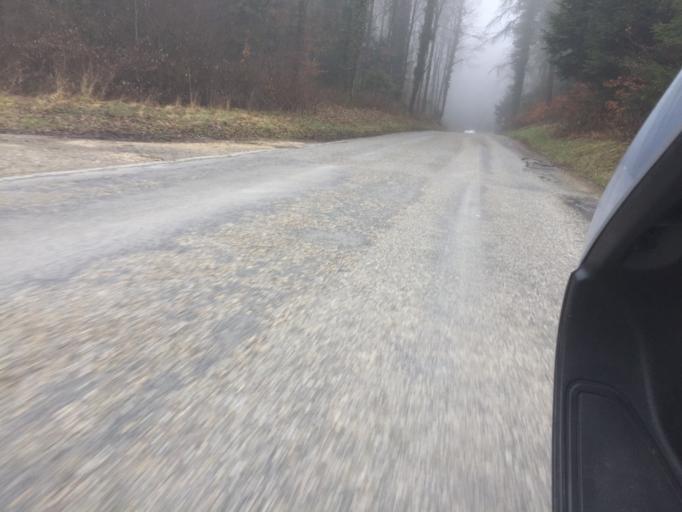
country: CH
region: Bern
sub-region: Seeland District
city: Grossaffoltern
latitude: 47.0963
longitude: 7.3670
